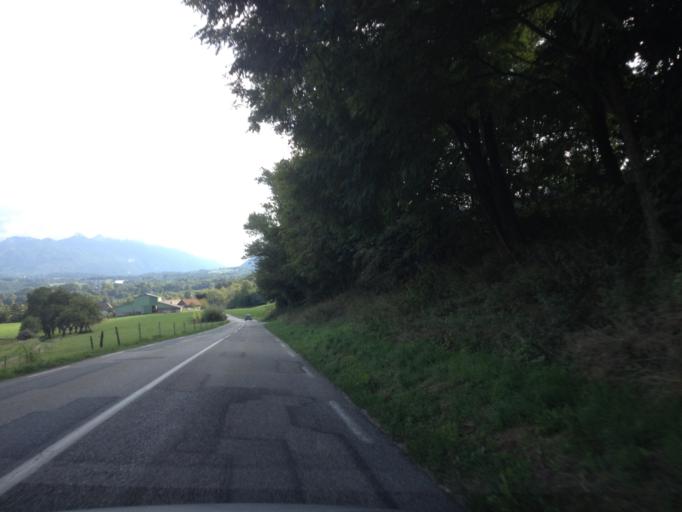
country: FR
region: Rhone-Alpes
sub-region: Departement de la Savoie
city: La Motte-Servolex
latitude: 45.6153
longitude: 5.8609
